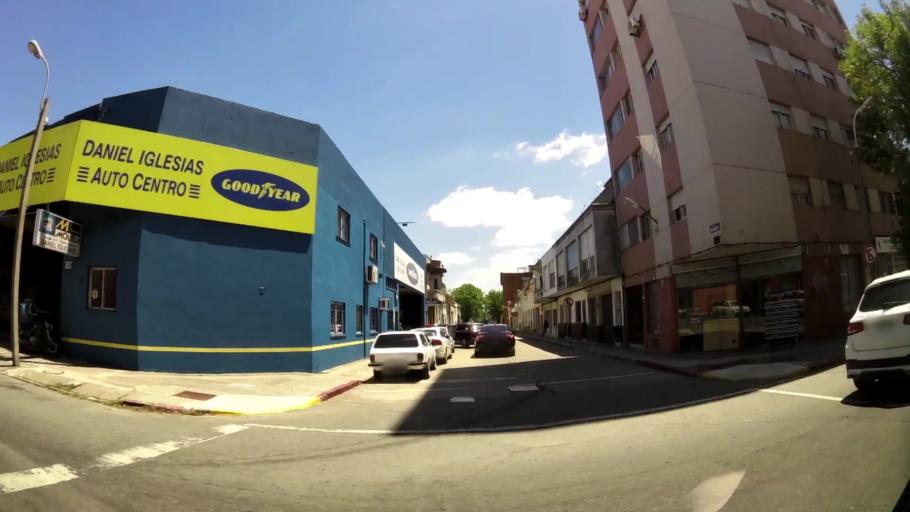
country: UY
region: Montevideo
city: Montevideo
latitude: -34.8955
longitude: -56.1811
